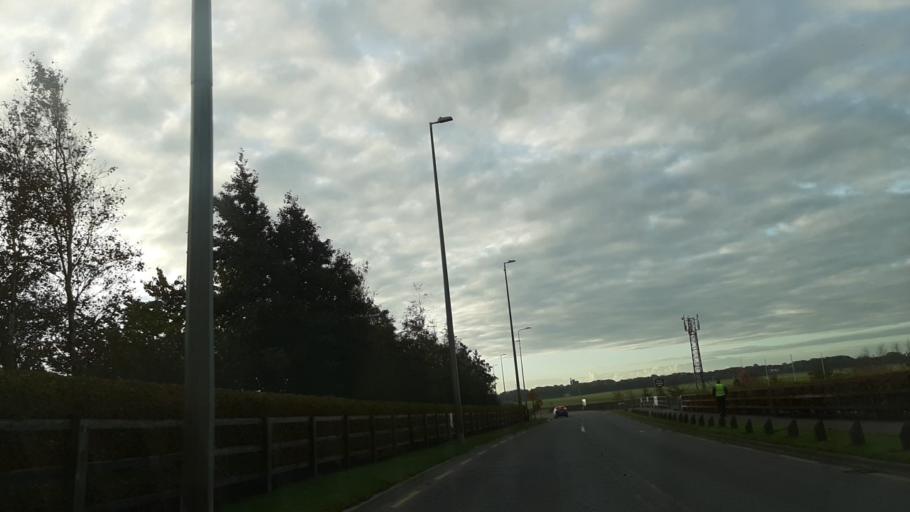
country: IE
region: Leinster
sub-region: Kildare
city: Athgarvan
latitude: 53.1684
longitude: -6.8394
